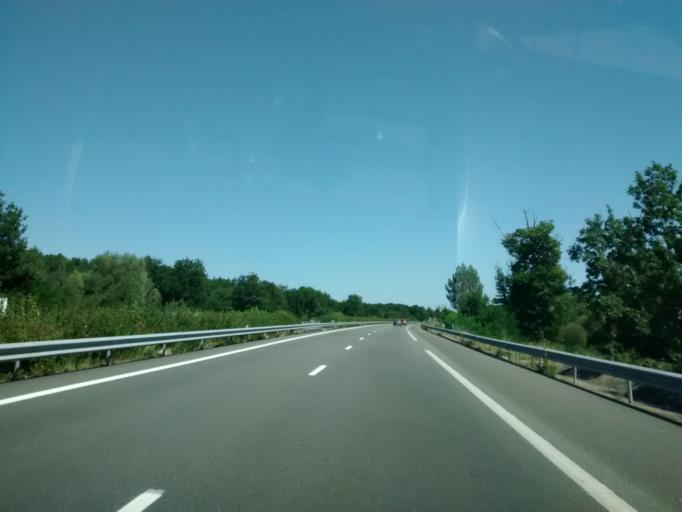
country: FR
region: Aquitaine
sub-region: Departement de la Dordogne
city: Menesplet
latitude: 44.9892
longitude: 0.0940
